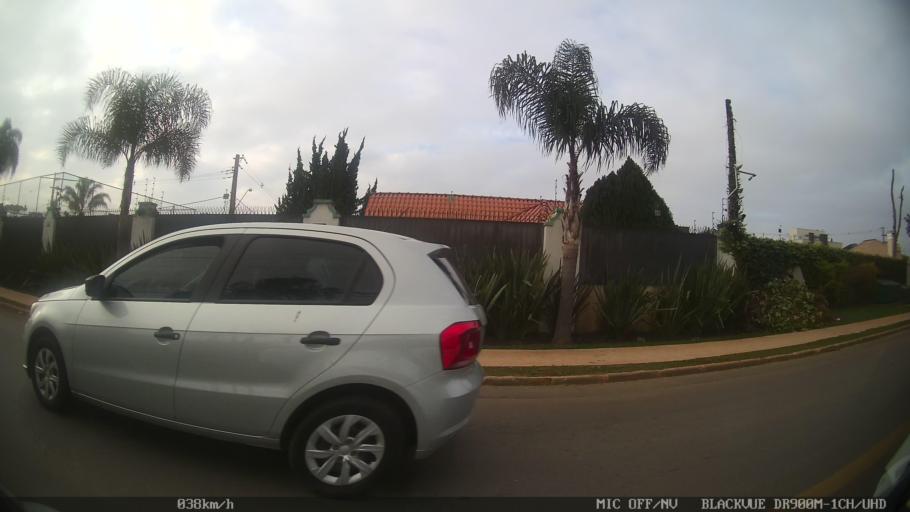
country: BR
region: Parana
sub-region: Almirante Tamandare
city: Almirante Tamandare
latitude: -25.3738
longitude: -49.3322
